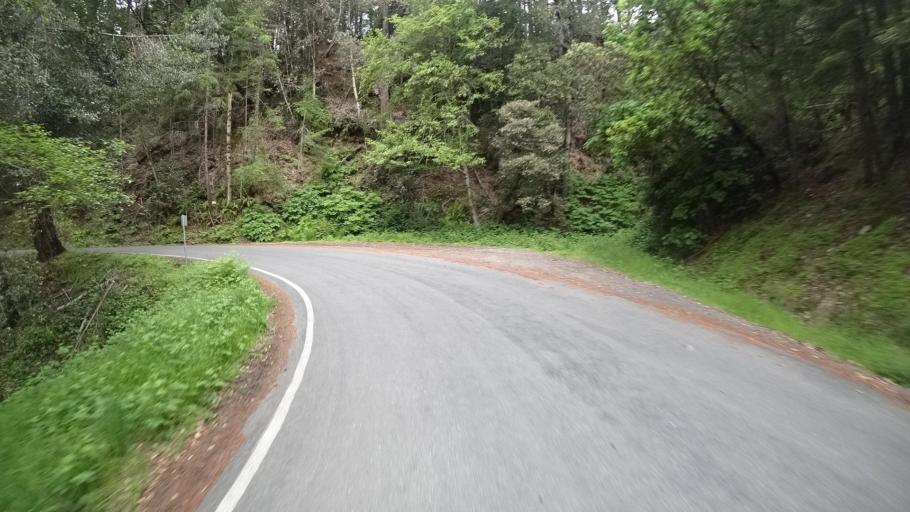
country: US
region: California
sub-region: Humboldt County
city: Willow Creek
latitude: 40.9501
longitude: -123.6193
